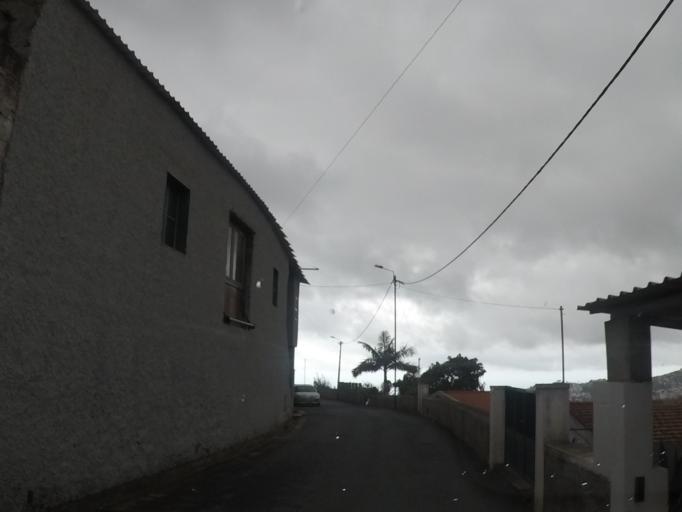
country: PT
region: Madeira
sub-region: Funchal
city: Nossa Senhora do Monte
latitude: 32.6719
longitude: -16.9138
